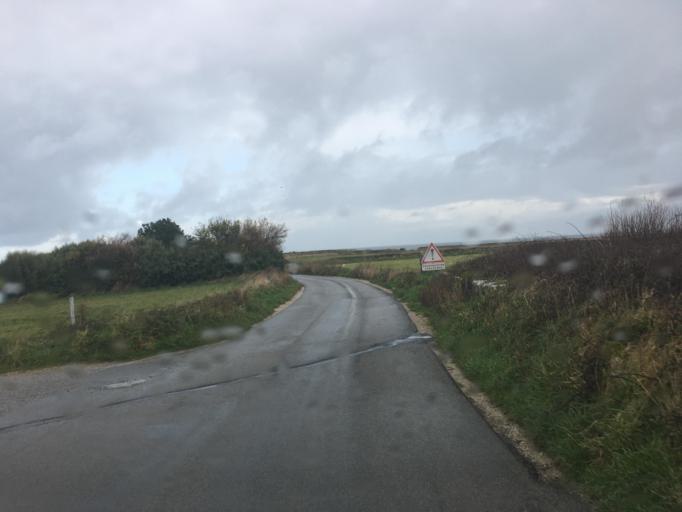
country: FR
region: Lower Normandy
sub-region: Departement de la Manche
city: Reville
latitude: 49.6920
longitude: -1.2776
